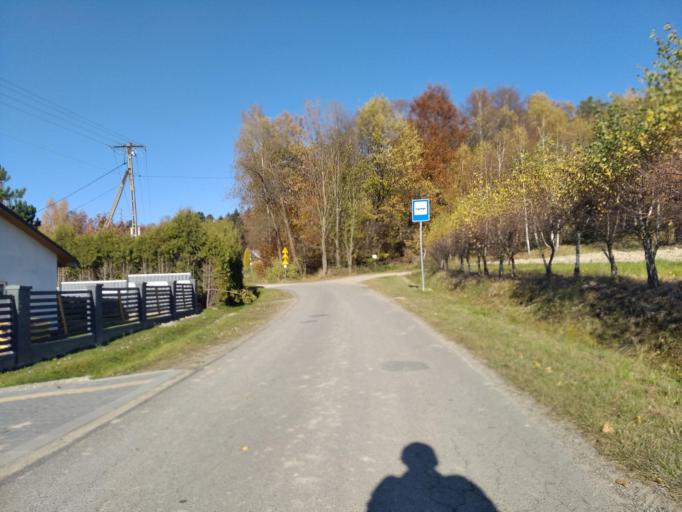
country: PL
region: Subcarpathian Voivodeship
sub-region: Powiat strzyzowski
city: Frysztak
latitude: 49.8539
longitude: 21.5914
